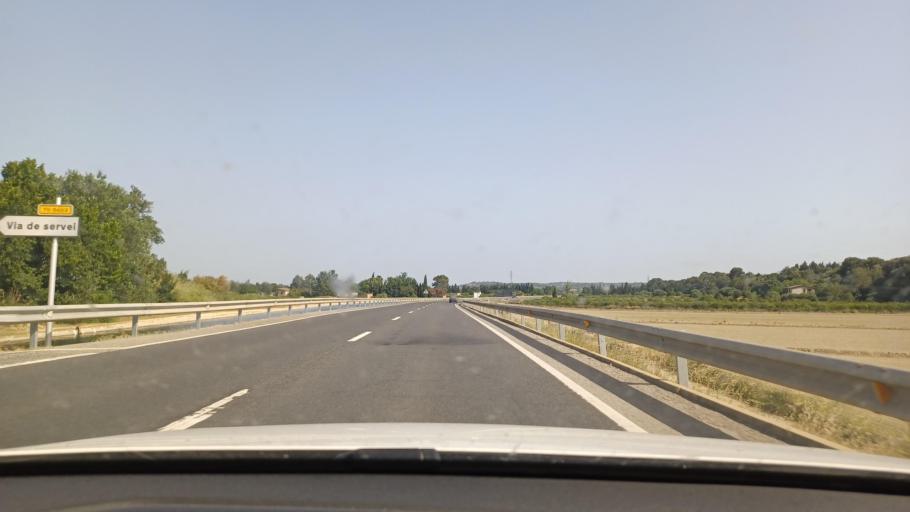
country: ES
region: Catalonia
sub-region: Provincia de Tarragona
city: Tortosa
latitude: 40.7727
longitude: 0.5281
